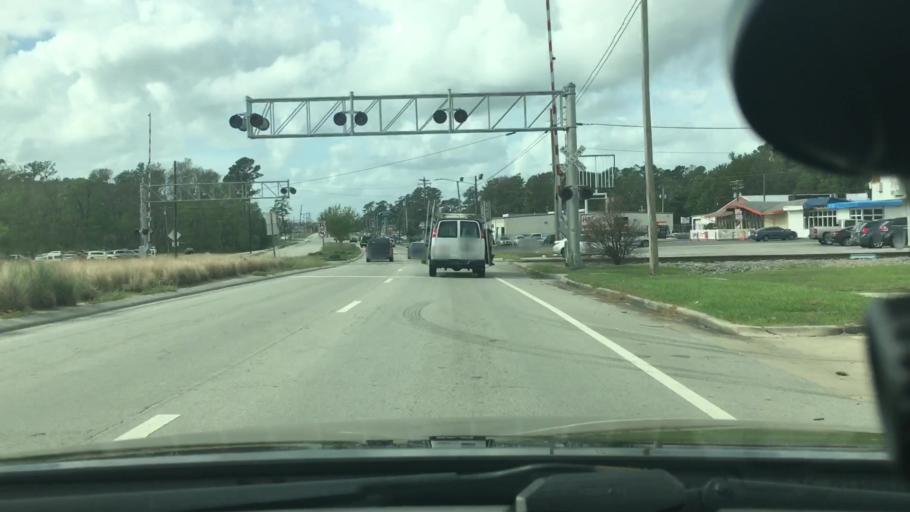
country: US
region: North Carolina
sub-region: Craven County
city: Havelock
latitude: 34.8806
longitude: -76.9066
